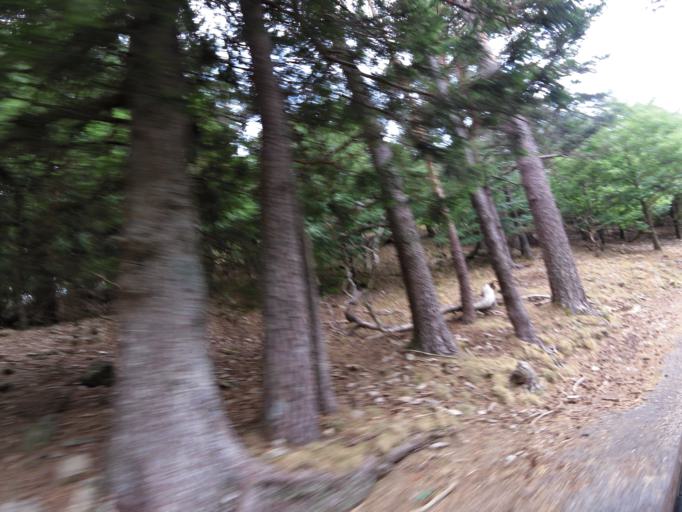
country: FR
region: Languedoc-Roussillon
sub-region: Departement du Gard
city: Valleraugue
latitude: 44.0489
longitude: 3.6092
